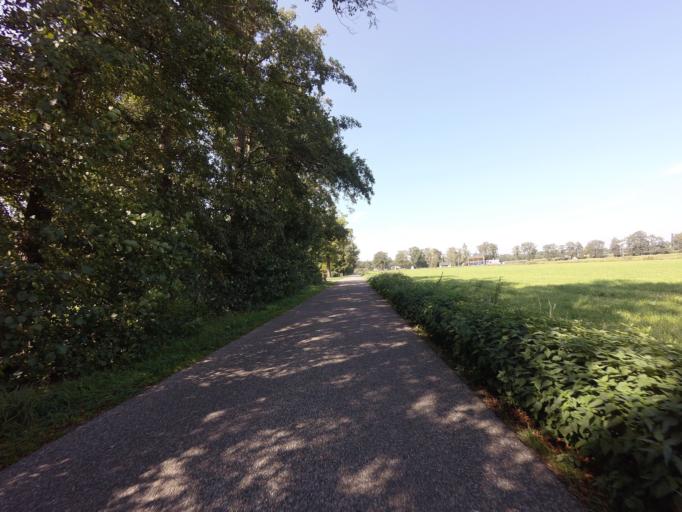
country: NL
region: Overijssel
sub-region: Gemeente Haaksbergen
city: Haaksbergen
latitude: 52.2121
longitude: 6.7562
